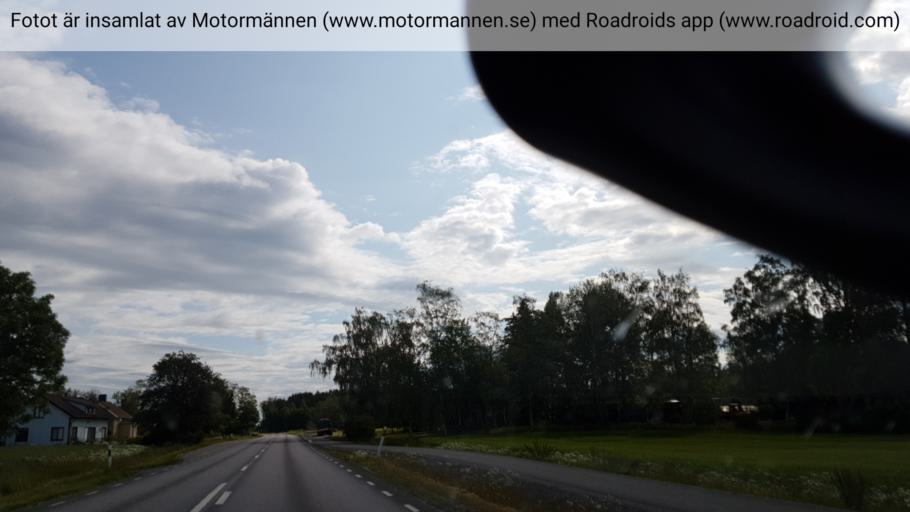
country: SE
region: Vaestra Goetaland
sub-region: Grastorps Kommun
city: Graestorp
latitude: 58.3336
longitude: 12.6136
